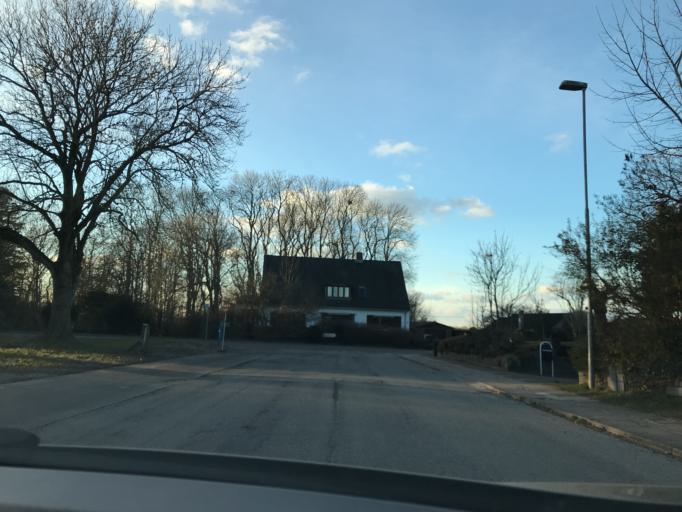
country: DK
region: South Denmark
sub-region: Middelfart Kommune
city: Norre Aby
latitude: 55.4547
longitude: 9.8687
